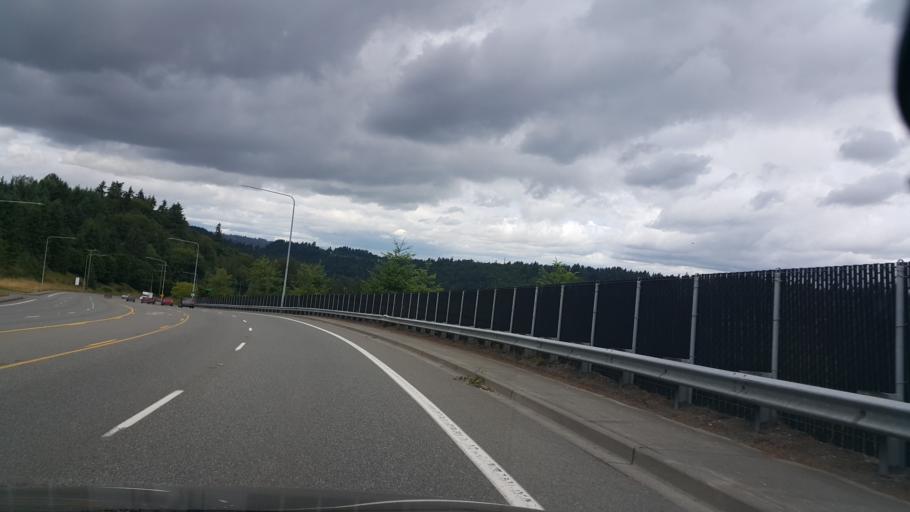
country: US
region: Washington
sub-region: King County
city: Fairwood
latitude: 47.4630
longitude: -122.1476
